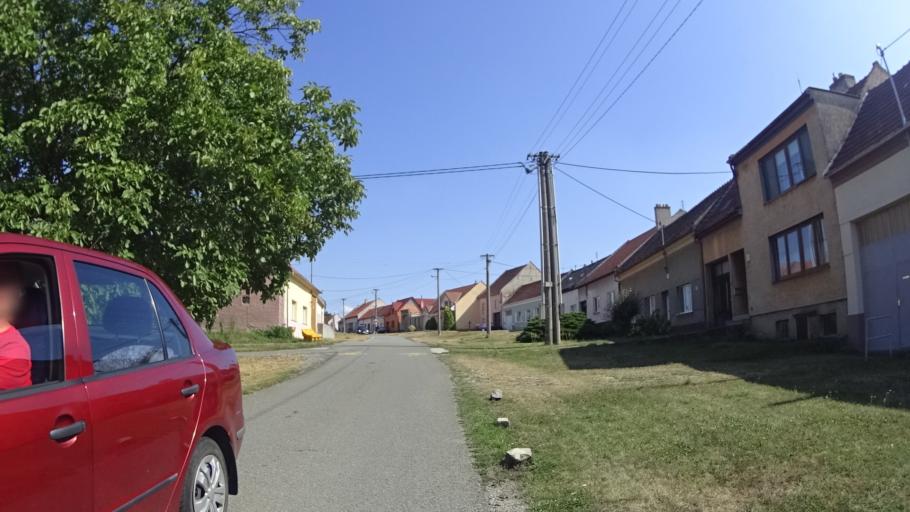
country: CZ
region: Zlin
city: Uhersky Ostroh
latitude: 48.9912
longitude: 17.4076
